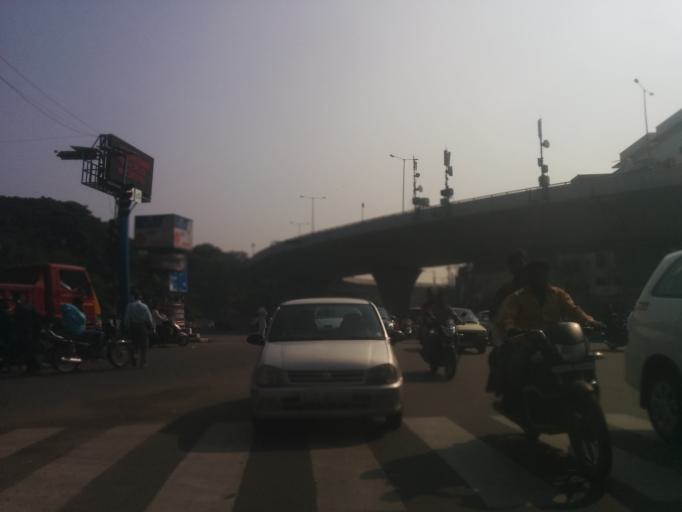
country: IN
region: Telangana
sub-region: Hyderabad
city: Hyderabad
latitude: 17.3958
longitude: 78.4310
